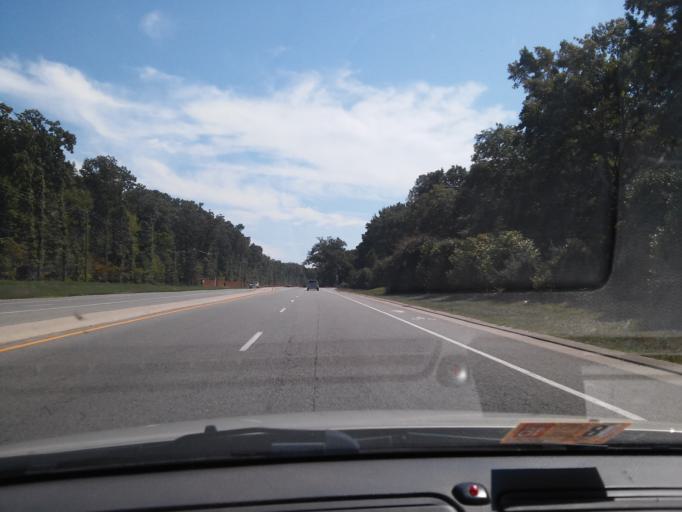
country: US
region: Virginia
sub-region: Chesterfield County
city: Bon Air
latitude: 37.5405
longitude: -77.6433
